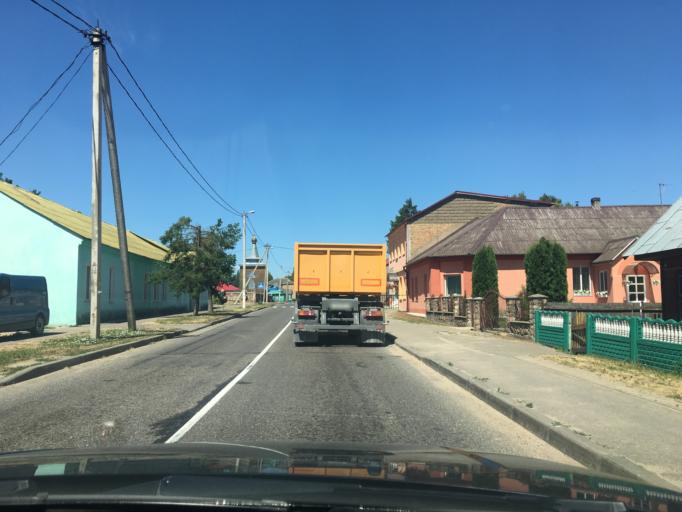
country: BY
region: Grodnenskaya
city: Hal'shany
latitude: 54.1575
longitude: 25.9073
